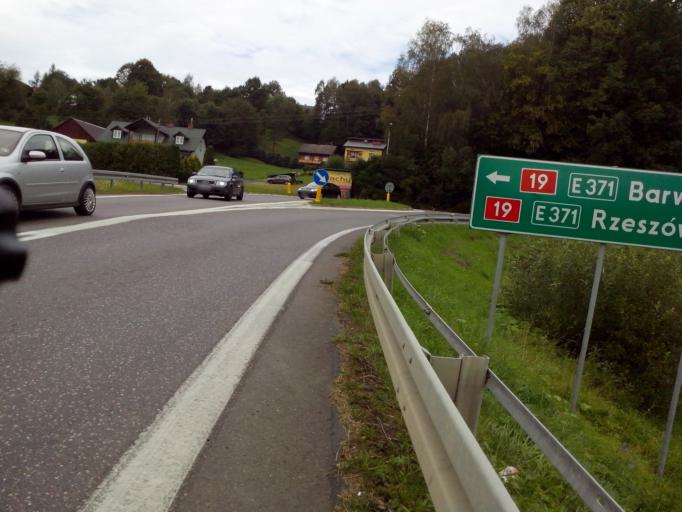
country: PL
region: Subcarpathian Voivodeship
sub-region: Powiat brzozowski
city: Domaradz
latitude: 49.7734
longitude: 21.9450
